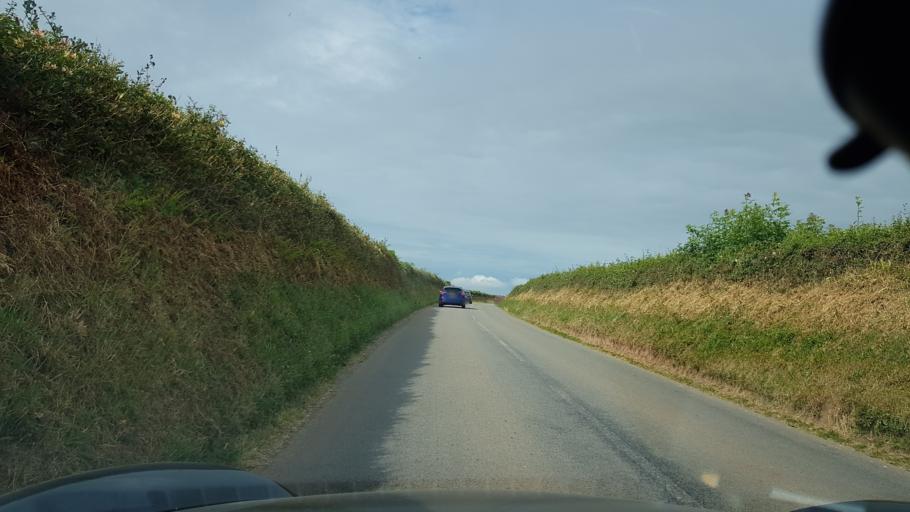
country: GB
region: Wales
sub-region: Pembrokeshire
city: Dale
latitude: 51.7423
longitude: -5.1503
